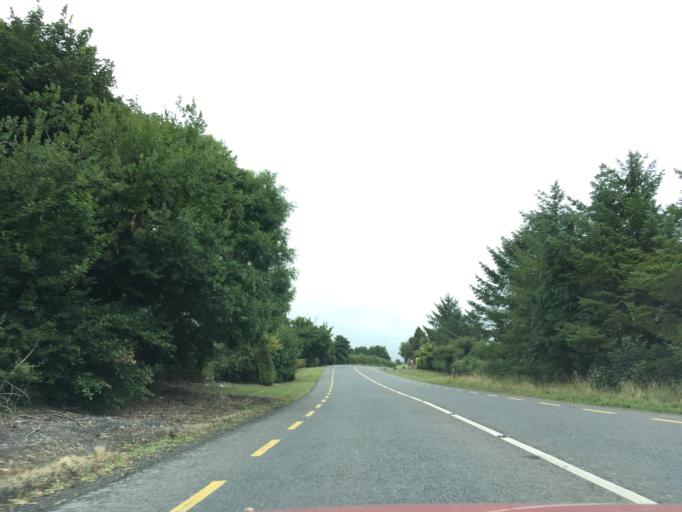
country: IE
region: Munster
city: Carrick-on-Suir
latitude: 52.3650
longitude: -7.5402
